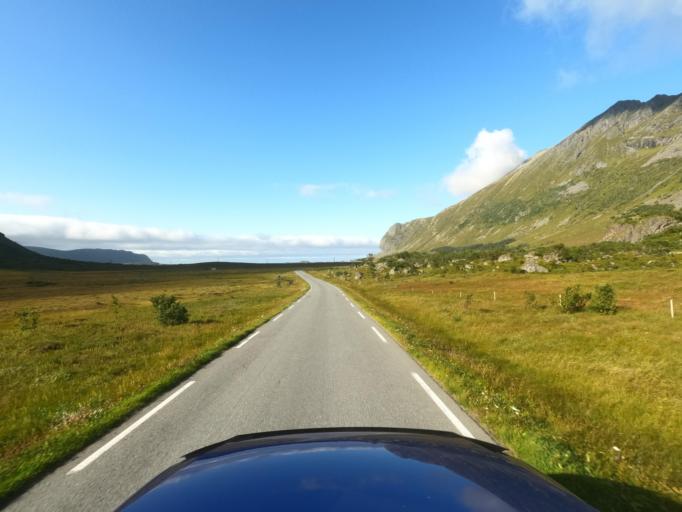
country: NO
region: Nordland
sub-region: Flakstad
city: Ramberg
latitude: 68.0679
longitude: 13.2367
